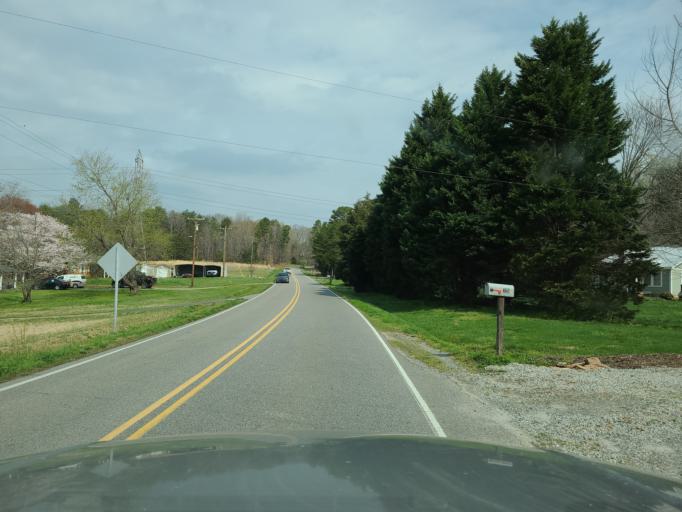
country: US
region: North Carolina
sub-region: Gaston County
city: Ranlo
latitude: 35.3160
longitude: -81.1056
